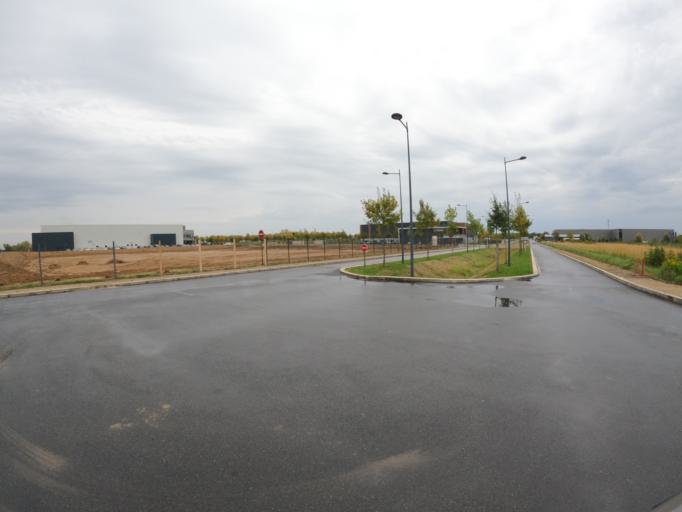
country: FR
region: Ile-de-France
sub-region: Departement de Seine-et-Marne
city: Serris
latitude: 48.8349
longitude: 2.7814
